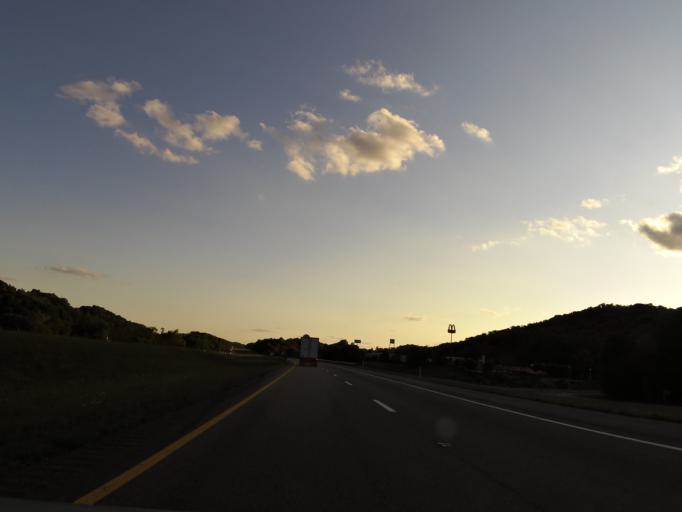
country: US
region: Tennessee
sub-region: Sullivan County
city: Blountville
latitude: 36.5350
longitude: -82.3860
